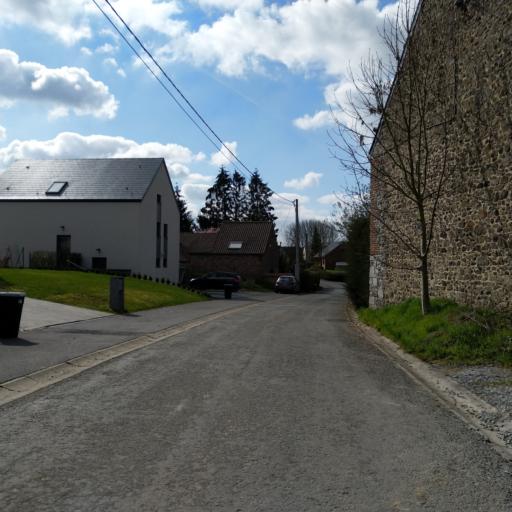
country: BE
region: Wallonia
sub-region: Province du Hainaut
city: Lens
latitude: 50.5615
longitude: 3.9421
